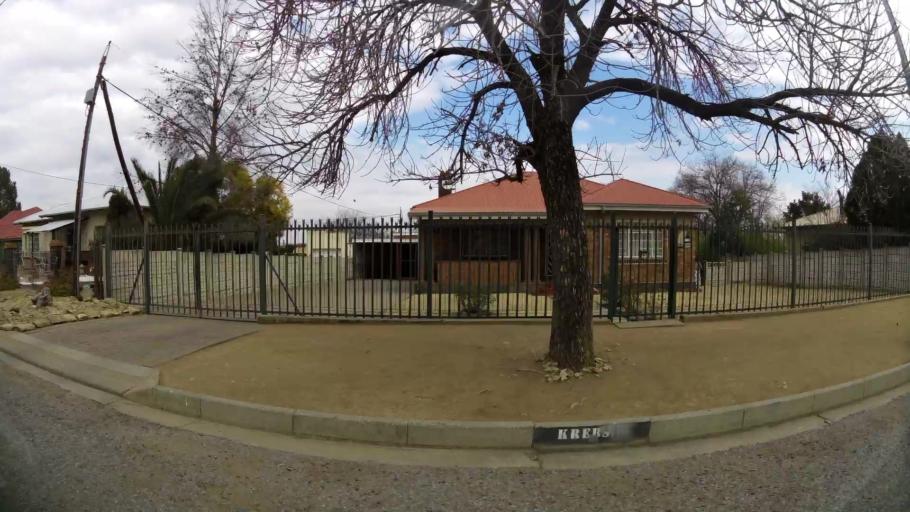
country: ZA
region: Orange Free State
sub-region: Fezile Dabi District Municipality
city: Kroonstad
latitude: -27.6499
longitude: 27.2334
